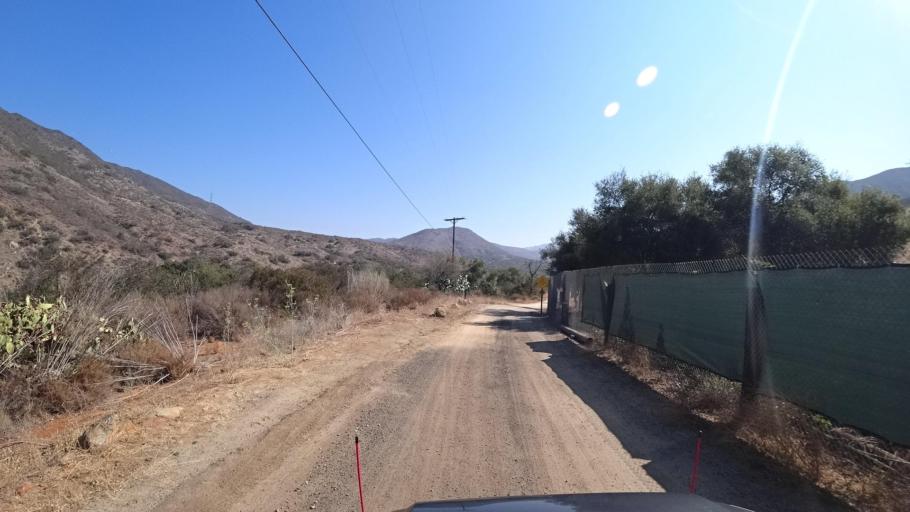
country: US
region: California
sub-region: San Diego County
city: Rainbow
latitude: 33.4256
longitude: -117.2015
